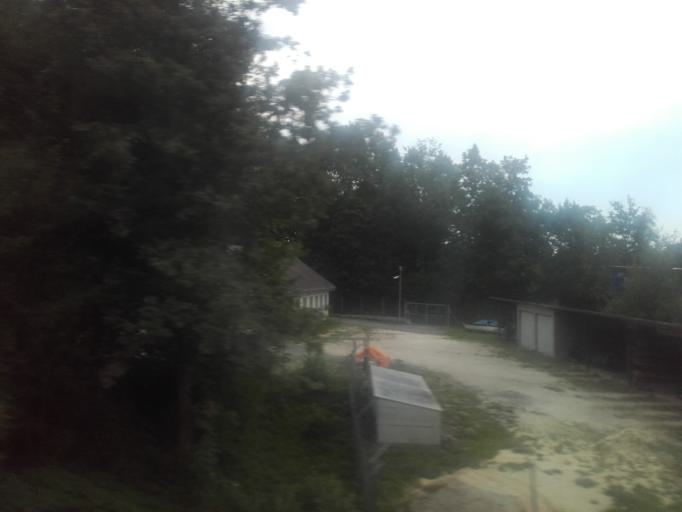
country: CH
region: Bern
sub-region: Emmental District
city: Kirchberg
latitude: 47.0896
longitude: 7.5720
